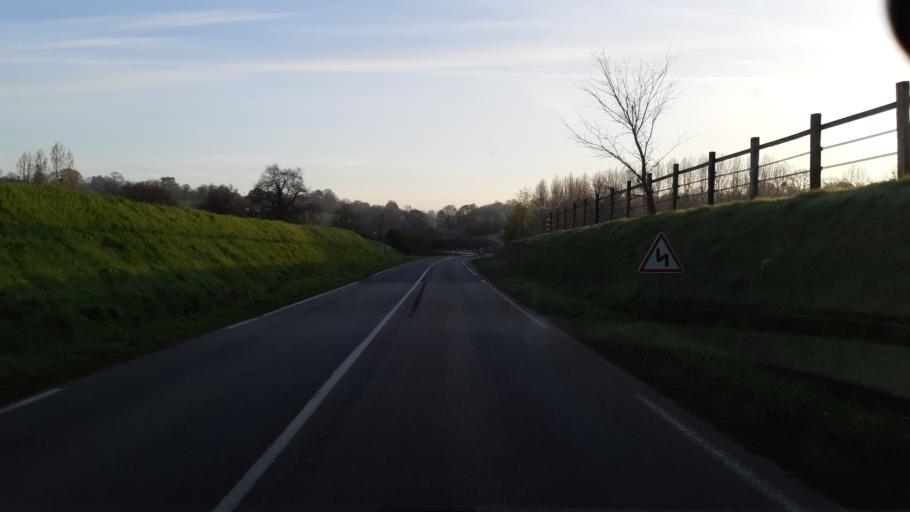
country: FR
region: Lower Normandy
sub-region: Departement de la Manche
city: Agneaux
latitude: 49.0673
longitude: -1.1313
